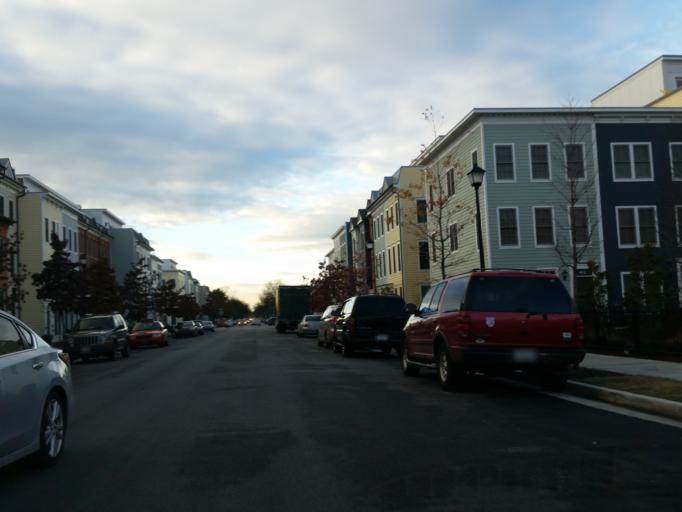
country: US
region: Virginia
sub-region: City of Alexandria
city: Alexandria
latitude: 38.8144
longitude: -77.0473
